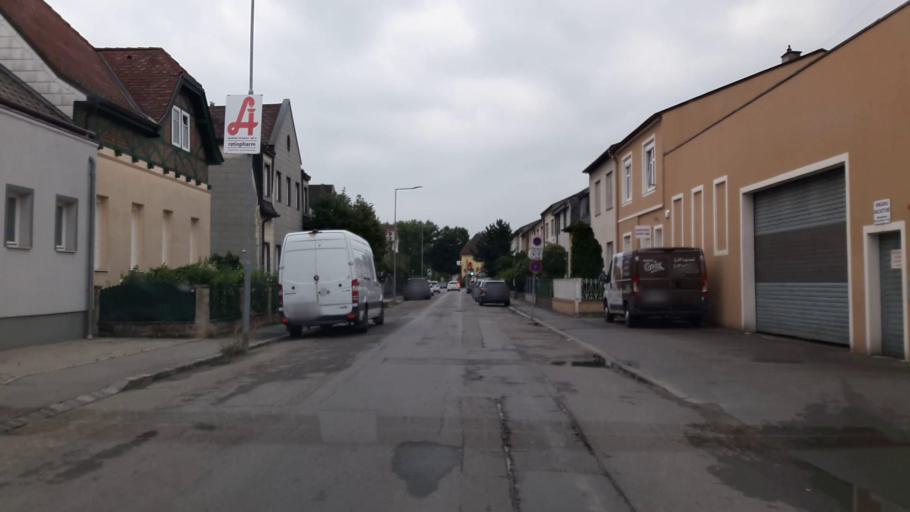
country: AT
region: Lower Austria
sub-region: Politischer Bezirk Ganserndorf
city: Strasshof an der Nordbahn
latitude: 48.3172
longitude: 16.6359
